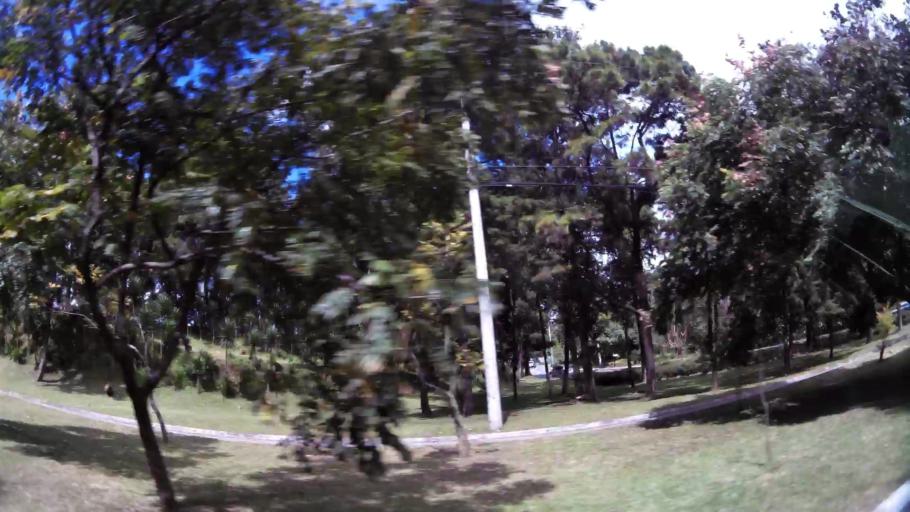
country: GT
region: Guatemala
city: Guatemala City
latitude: 14.6116
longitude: -90.5063
